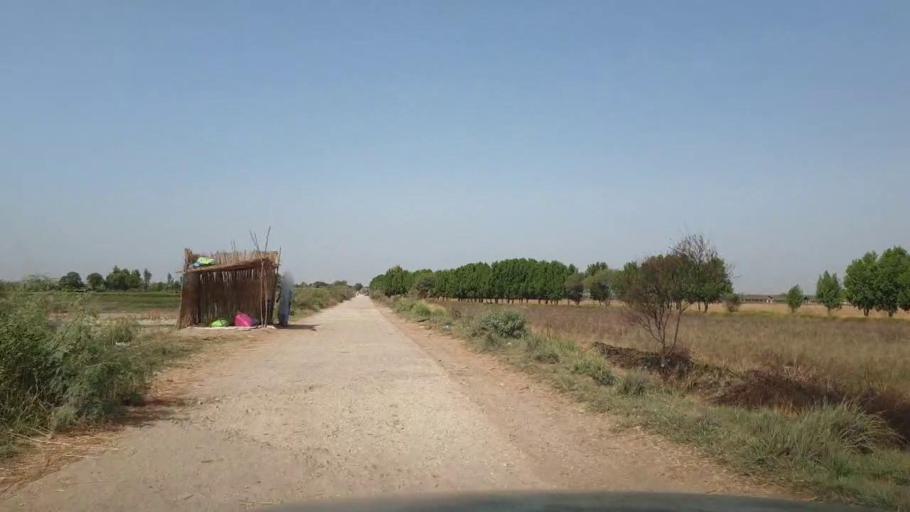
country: PK
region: Sindh
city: Tando Muhammad Khan
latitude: 25.1559
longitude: 68.3956
